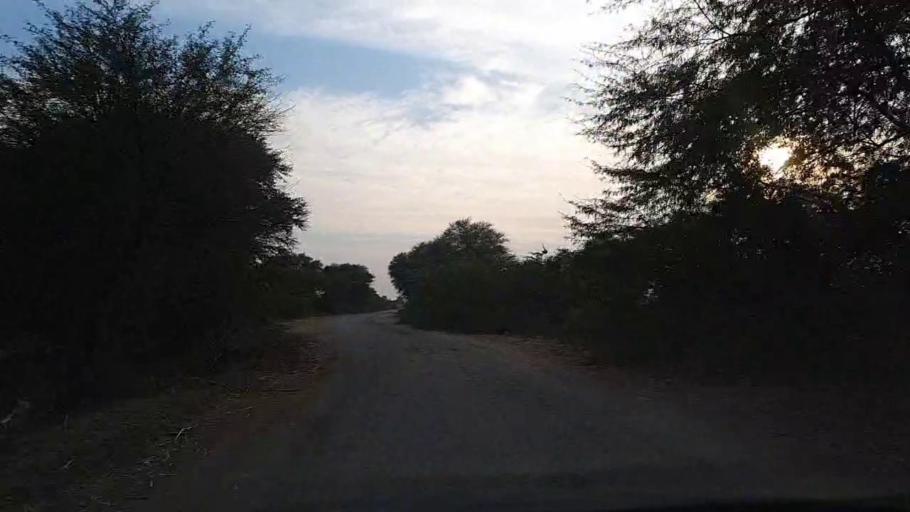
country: PK
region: Sindh
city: Nawabshah
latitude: 26.4017
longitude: 68.4817
